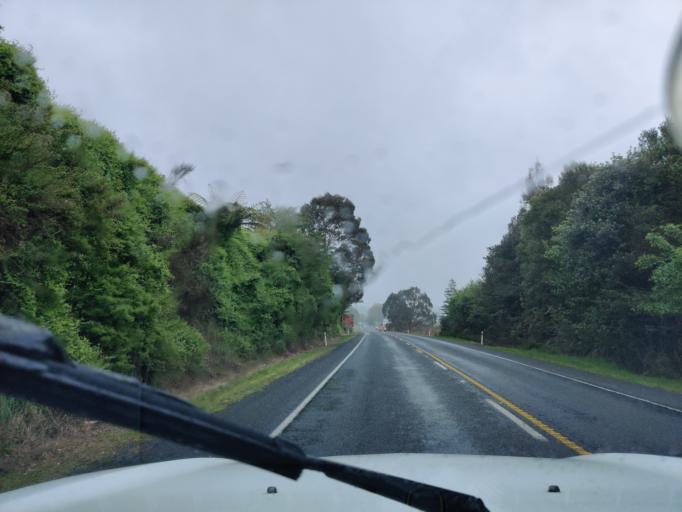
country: NZ
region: Bay of Plenty
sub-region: Rotorua District
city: Rotorua
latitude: -38.0886
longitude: 176.2064
